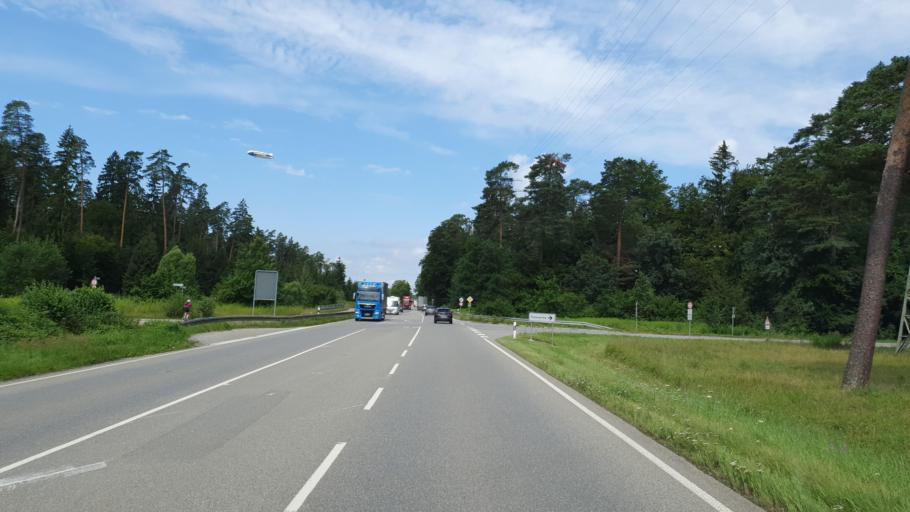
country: DE
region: Baden-Wuerttemberg
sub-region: Tuebingen Region
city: Eriskirch
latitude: 47.6235
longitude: 9.5551
